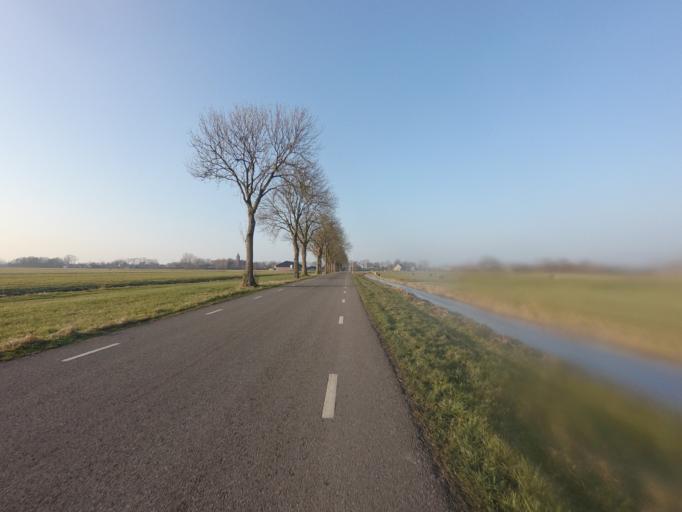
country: NL
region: South Holland
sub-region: Gemeente Vlist
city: Vlist
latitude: 52.0086
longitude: 4.8096
